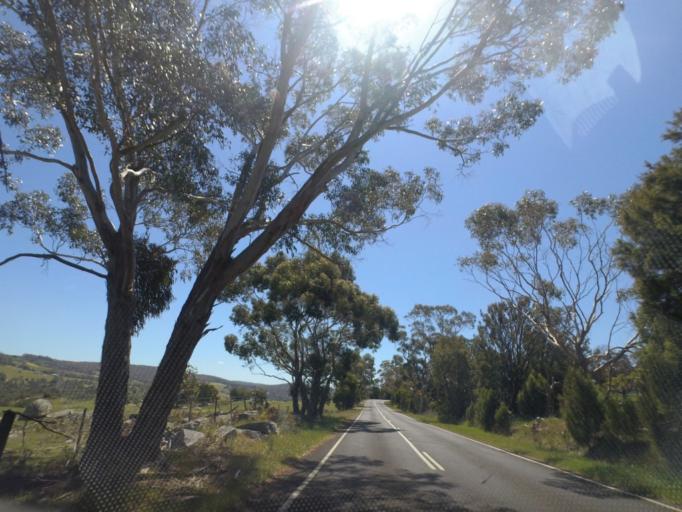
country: AU
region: Victoria
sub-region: Hume
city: Sunbury
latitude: -37.1996
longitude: 144.7400
